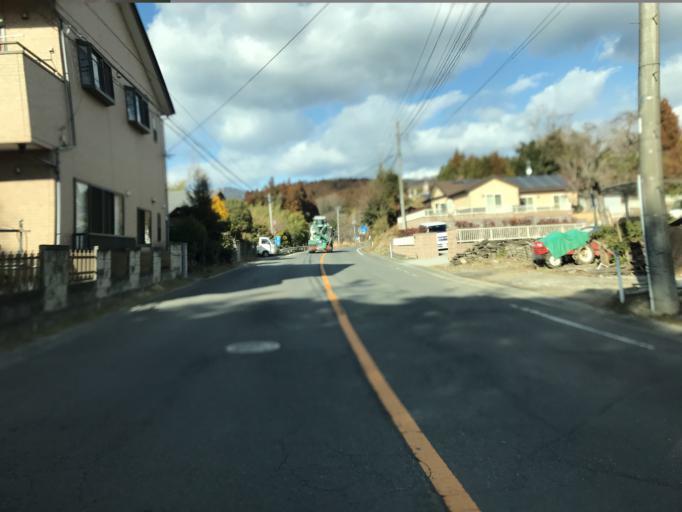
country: JP
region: Fukushima
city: Iwaki
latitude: 37.1197
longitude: 140.8713
